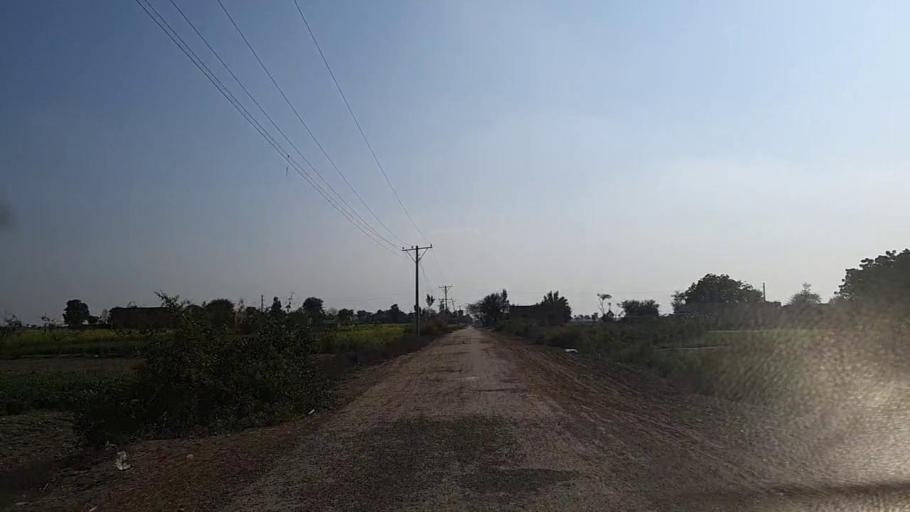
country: PK
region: Sindh
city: Jam Sahib
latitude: 26.2789
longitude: 68.6046
